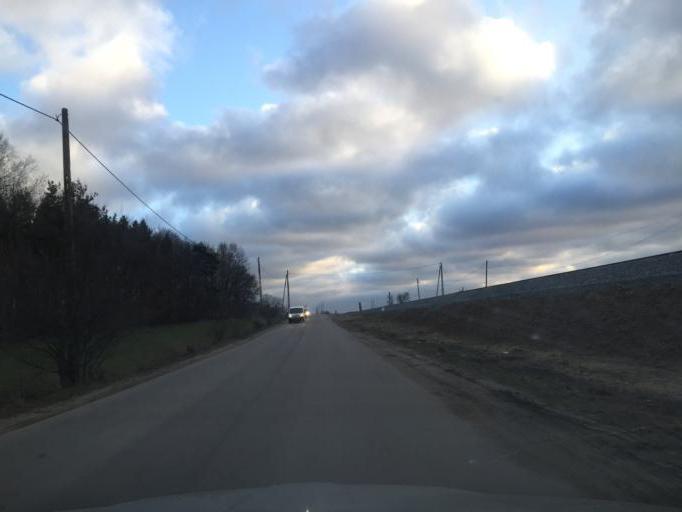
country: PL
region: Pomeranian Voivodeship
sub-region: Powiat kartuski
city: Banino
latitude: 54.4076
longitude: 18.4420
